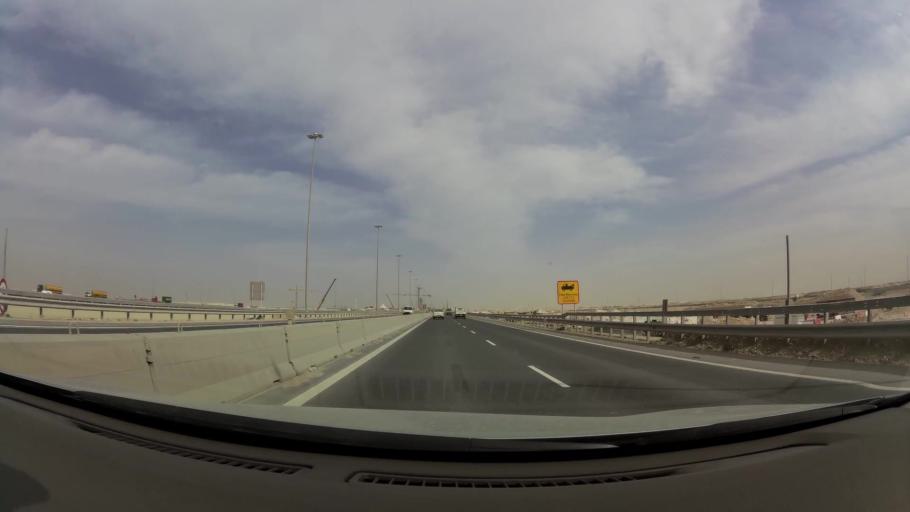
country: QA
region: Baladiyat ar Rayyan
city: Ash Shahaniyah
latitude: 25.3413
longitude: 51.3159
